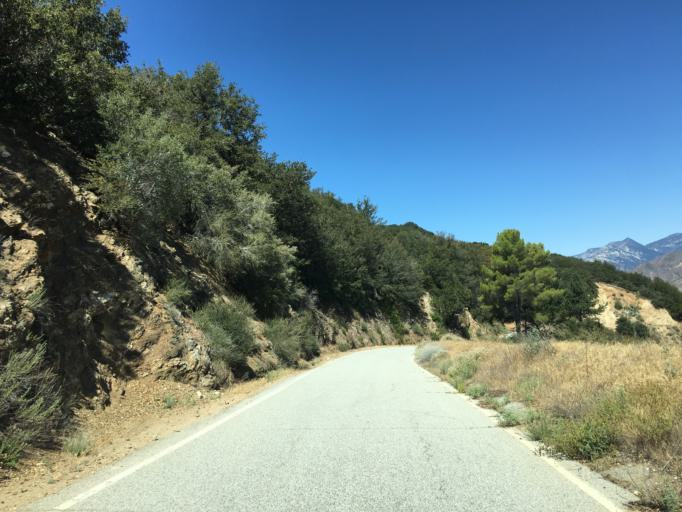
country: US
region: California
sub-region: San Bernardino County
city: San Antonio Heights
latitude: 34.2201
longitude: -117.7174
